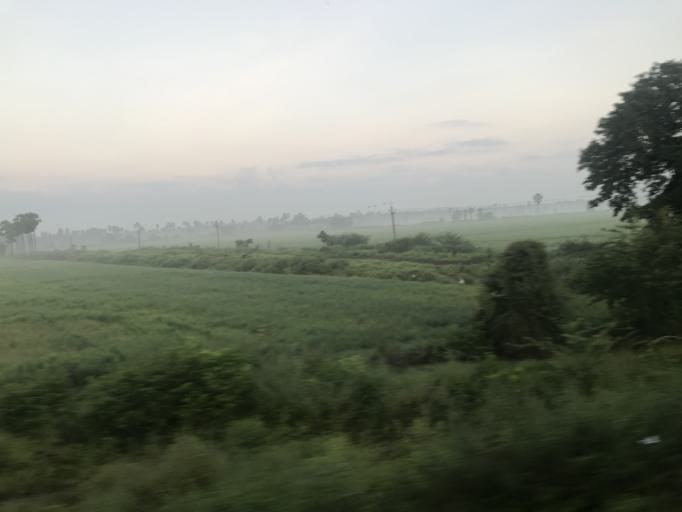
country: IN
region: Andhra Pradesh
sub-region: Guntur
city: Ponnur
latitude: 16.0854
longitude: 80.5653
